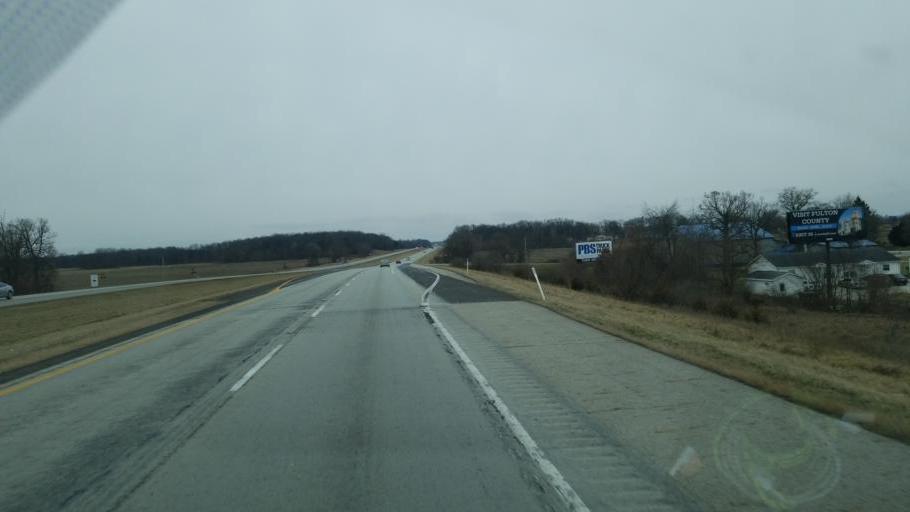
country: US
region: Indiana
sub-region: Fulton County
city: Rochester
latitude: 41.0779
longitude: -86.2404
